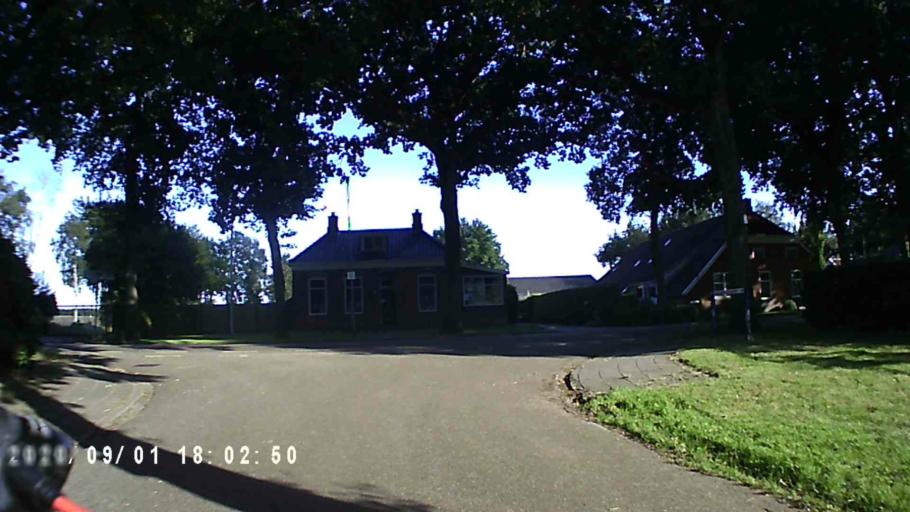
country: NL
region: Groningen
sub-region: Gemeente Slochteren
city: Slochteren
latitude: 53.1986
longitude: 6.7866
